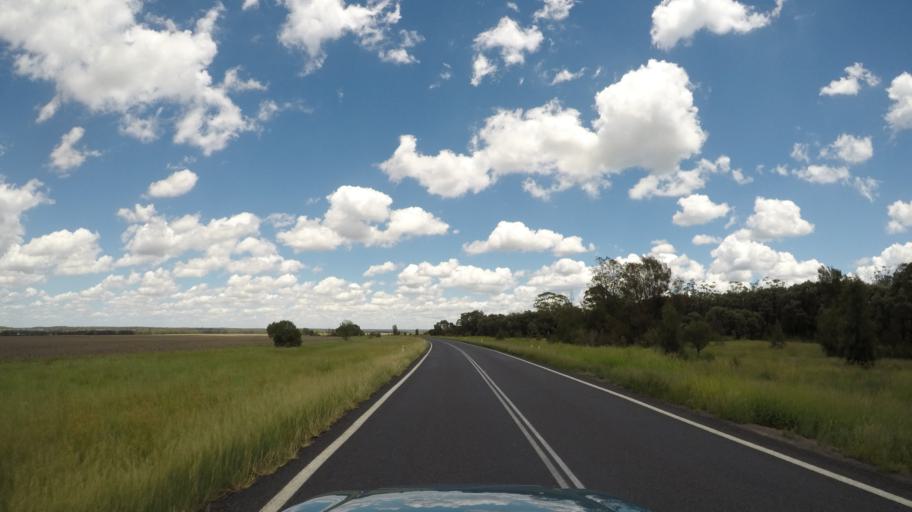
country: AU
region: Queensland
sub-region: Goondiwindi
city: Goondiwindi
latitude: -28.0008
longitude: 150.9020
